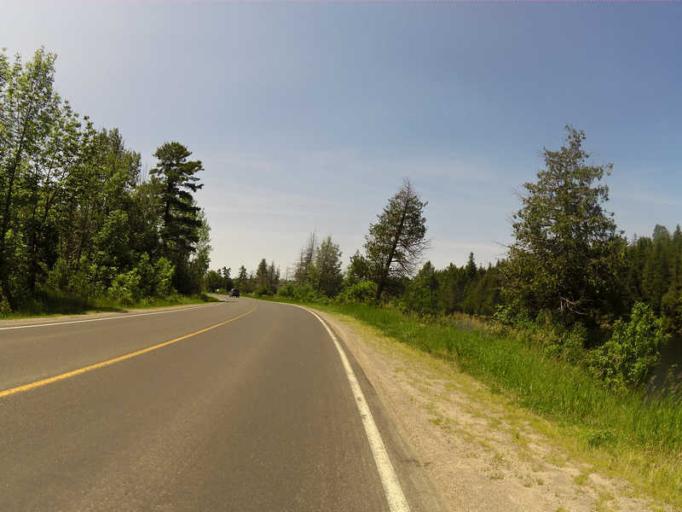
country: CA
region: Ontario
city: Peterborough
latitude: 44.3805
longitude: -78.2790
